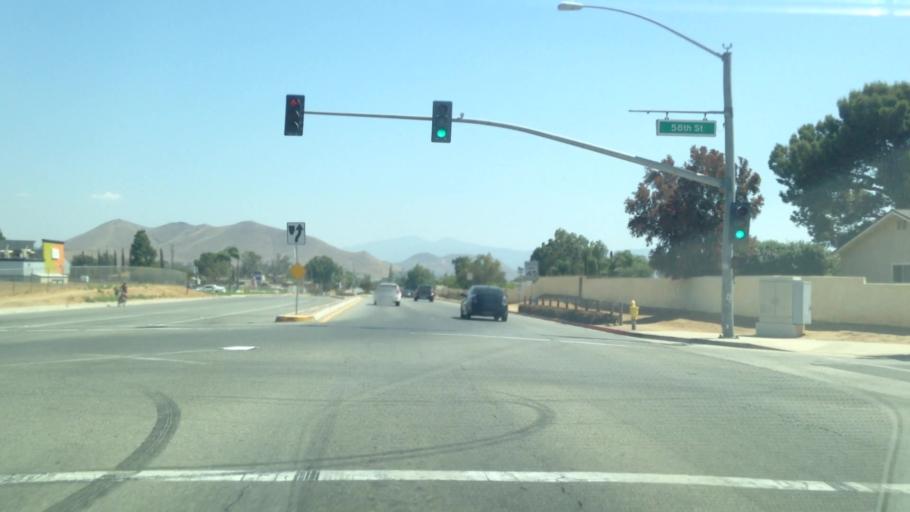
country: US
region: California
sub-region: Riverside County
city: Mira Loma
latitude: 33.9829
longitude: -117.5234
